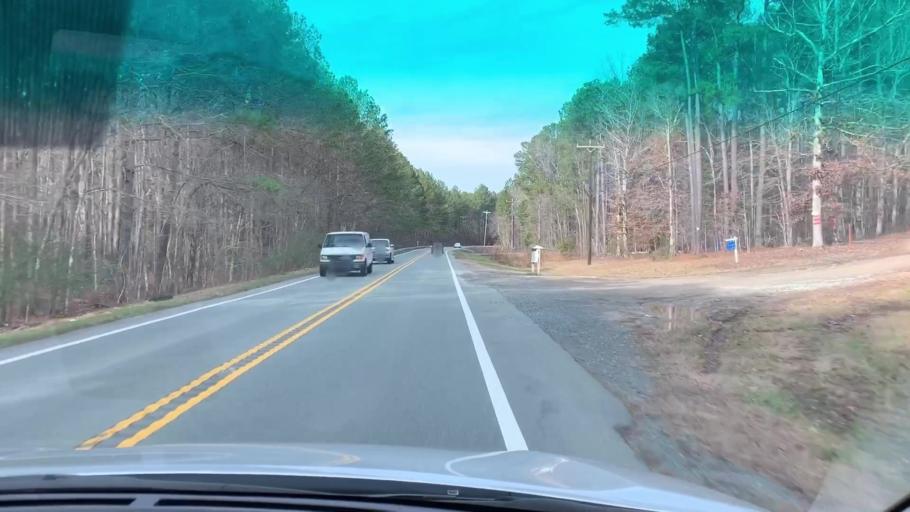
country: US
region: North Carolina
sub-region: Wake County
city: Green Level
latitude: 35.8505
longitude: -78.9352
